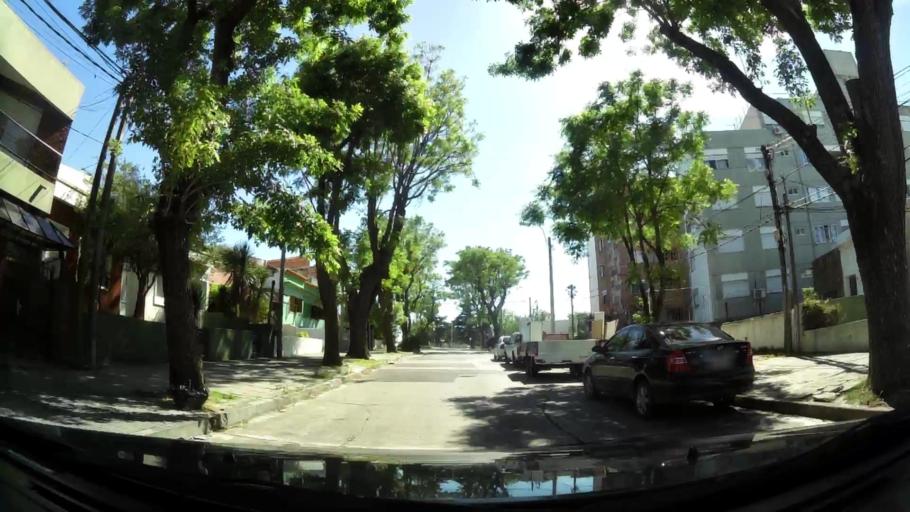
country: UY
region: Montevideo
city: Montevideo
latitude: -34.8893
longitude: -56.1257
